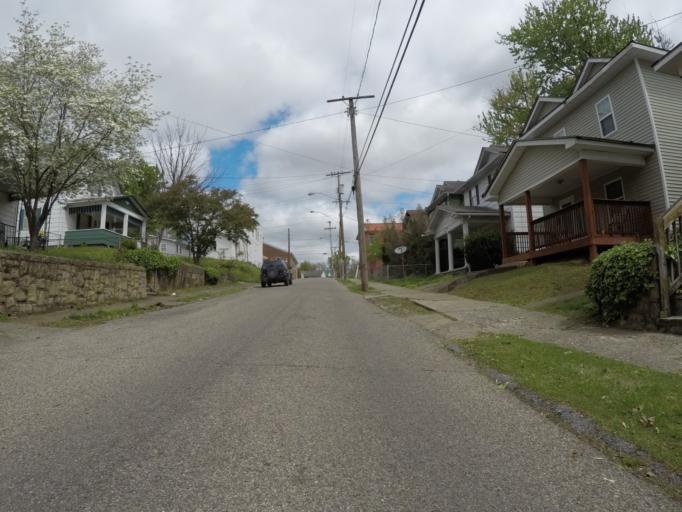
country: US
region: West Virginia
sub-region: Cabell County
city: Huntington
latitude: 38.4106
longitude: -82.4063
